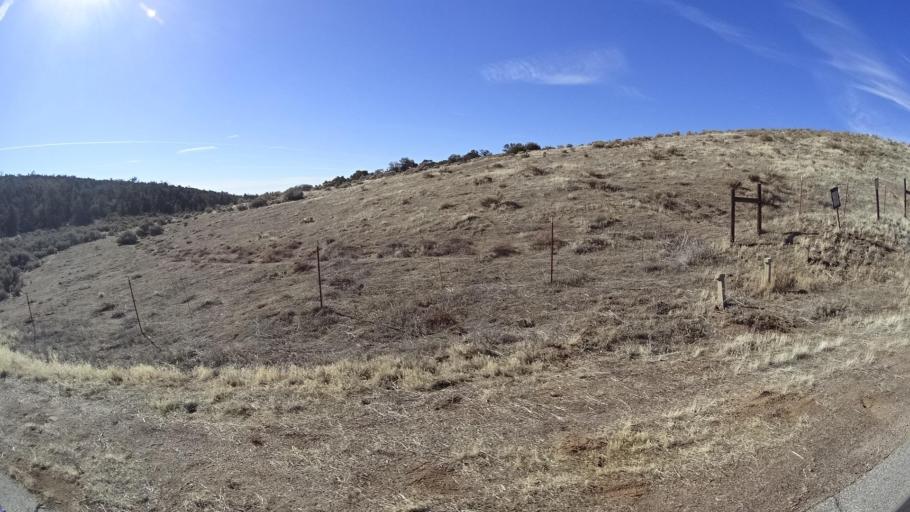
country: US
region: California
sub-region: Kern County
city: Pine Mountain Club
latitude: 34.8720
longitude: -119.2846
